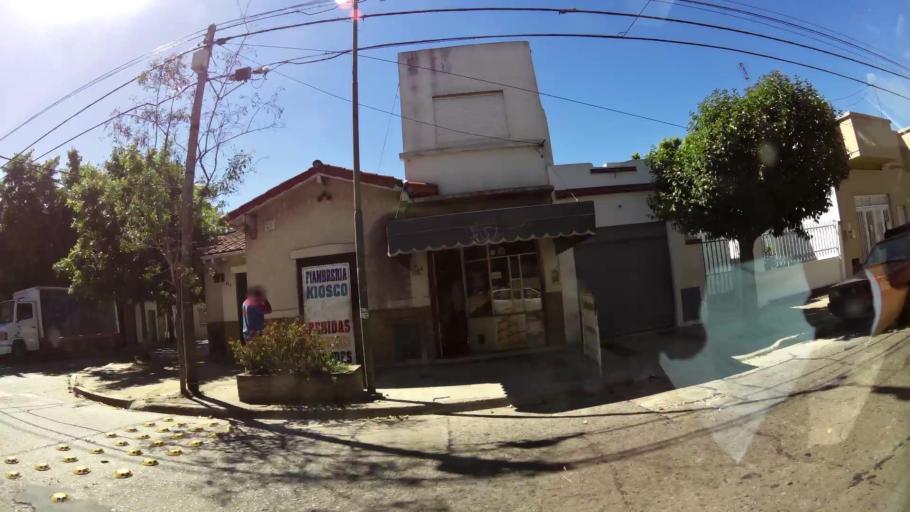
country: AR
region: Buenos Aires
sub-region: Partido de General San Martin
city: General San Martin
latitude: -34.5643
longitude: -58.5310
